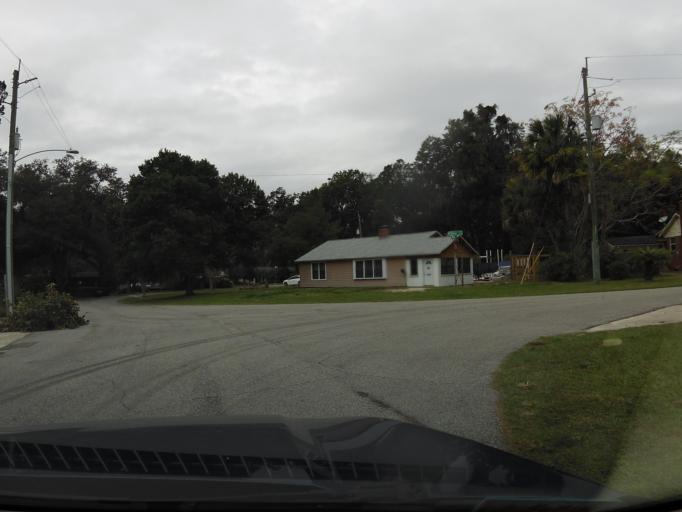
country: US
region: Florida
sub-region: Duval County
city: Jacksonville
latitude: 30.3064
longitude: -81.6071
